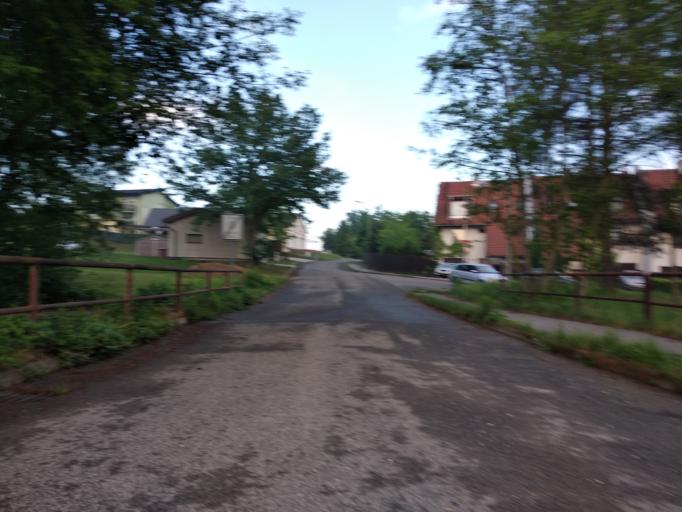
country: CZ
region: Moravskoslezsky
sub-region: Okres Frydek-Mistek
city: Stare Mesto
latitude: 49.6904
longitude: 18.3726
